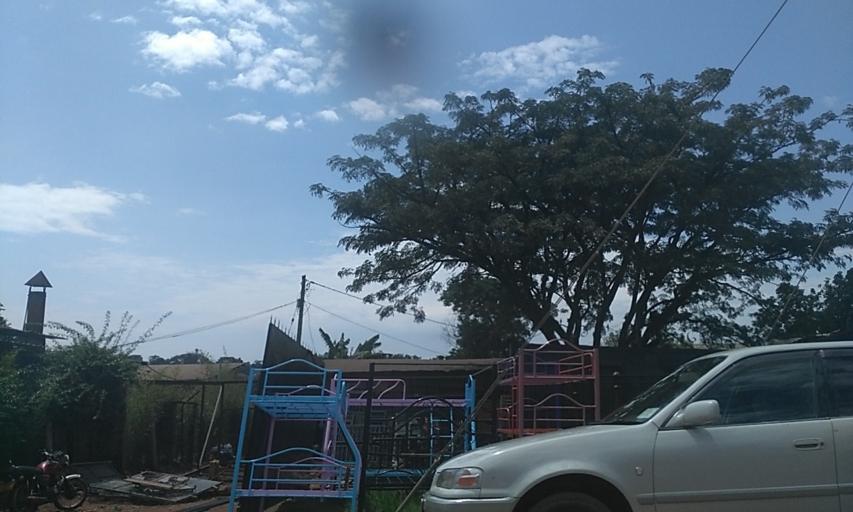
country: UG
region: Central Region
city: Kampala Central Division
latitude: 0.3898
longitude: 32.5929
